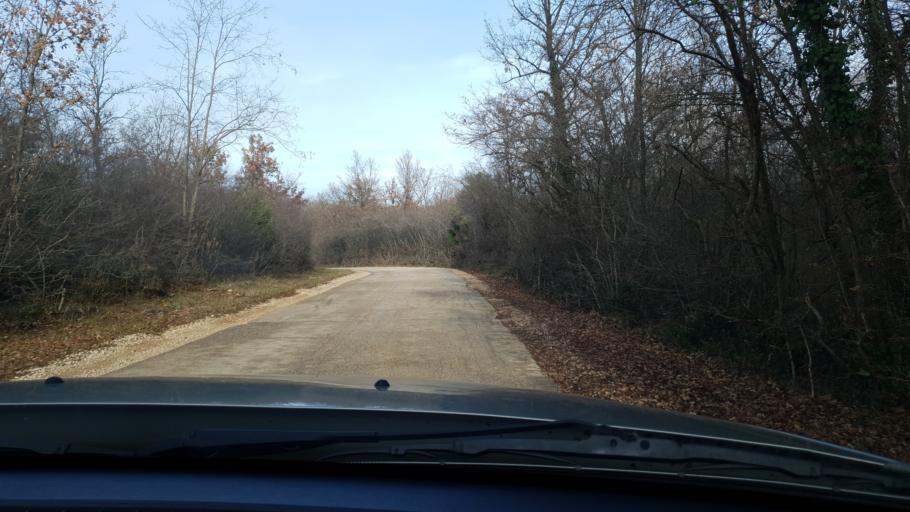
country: HR
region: Istarska
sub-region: Grad Porec
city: Porec
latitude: 45.2489
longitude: 13.6605
